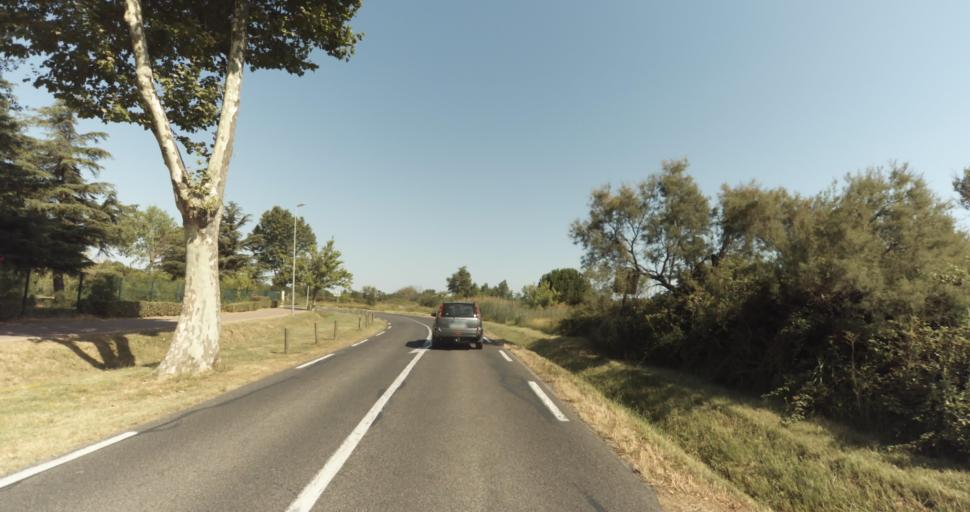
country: FR
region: Languedoc-Roussillon
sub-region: Departement des Pyrenees-Orientales
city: Saint-Cyprien-Plage
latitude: 42.6174
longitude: 3.0206
